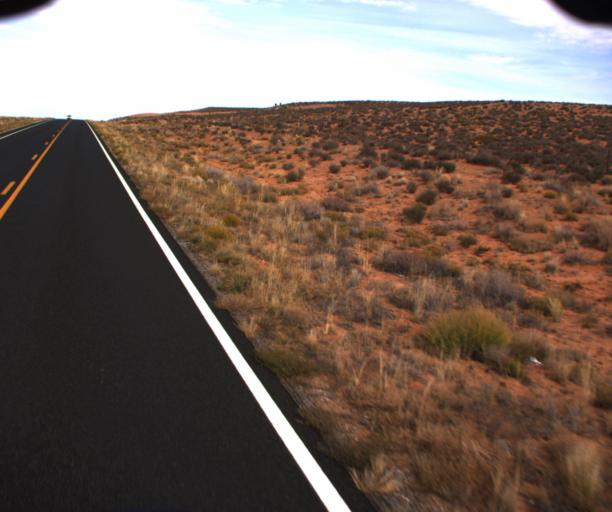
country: US
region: Arizona
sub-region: Apache County
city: Many Farms
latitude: 36.8808
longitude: -109.6292
